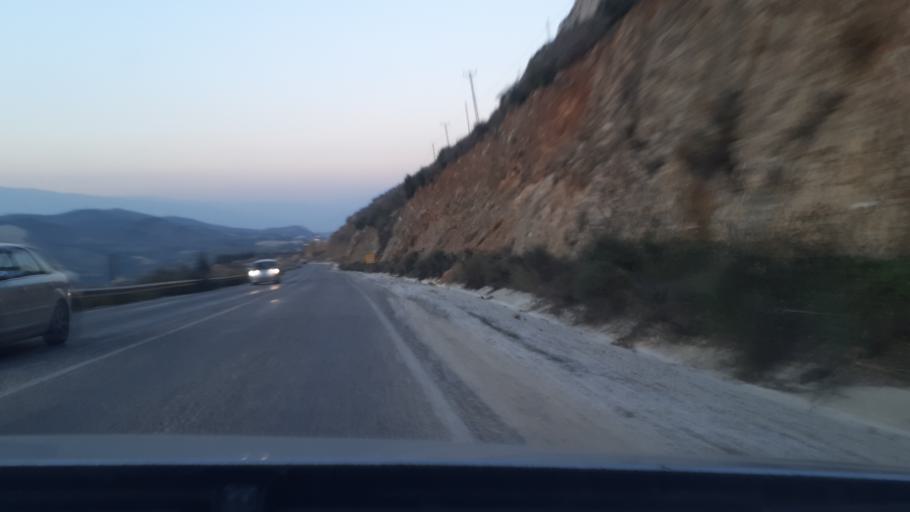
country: TR
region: Hatay
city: Dursunlu
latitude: 36.1696
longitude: 36.1863
